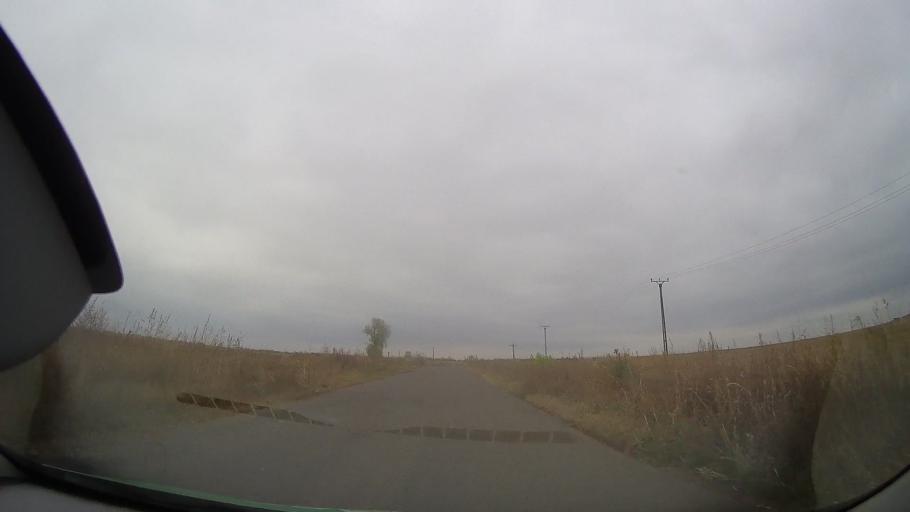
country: RO
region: Braila
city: Dudesti
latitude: 44.9324
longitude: 27.4270
